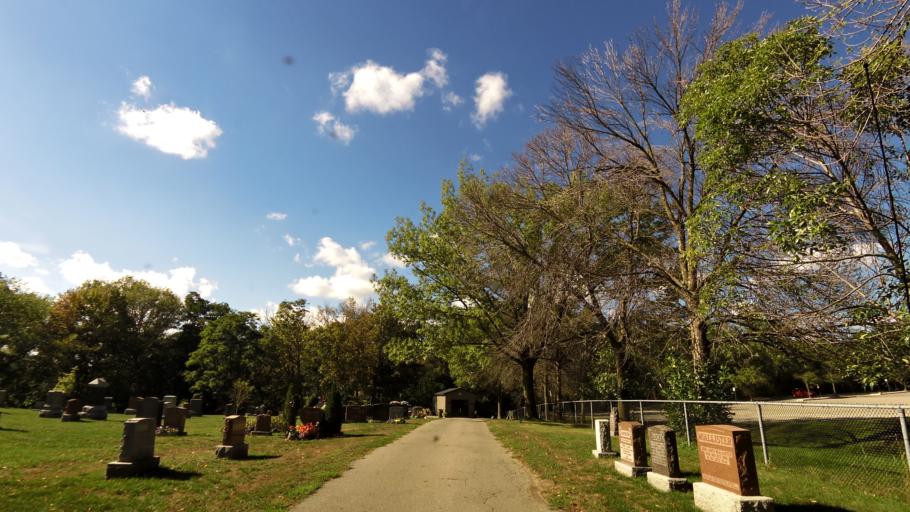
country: CA
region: Ontario
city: Mississauga
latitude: 43.5797
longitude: -79.7032
